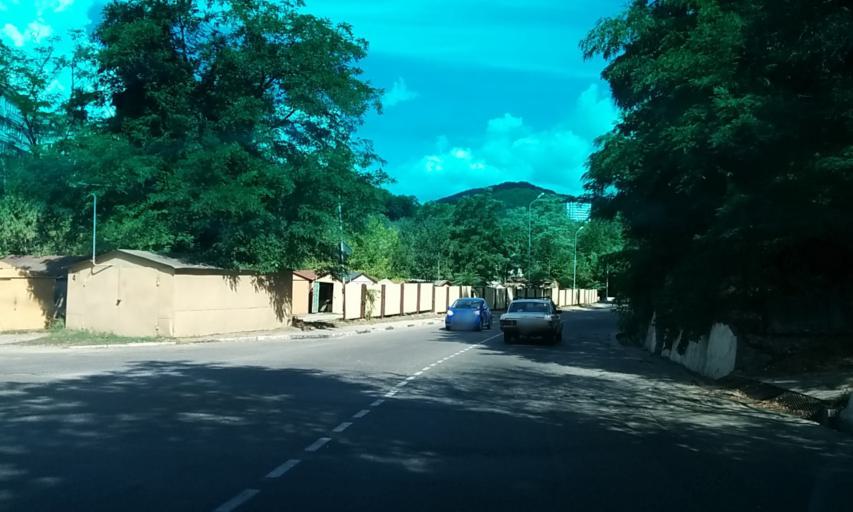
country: RU
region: Krasnodarskiy
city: Tuapse
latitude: 44.1097
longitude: 39.0622
